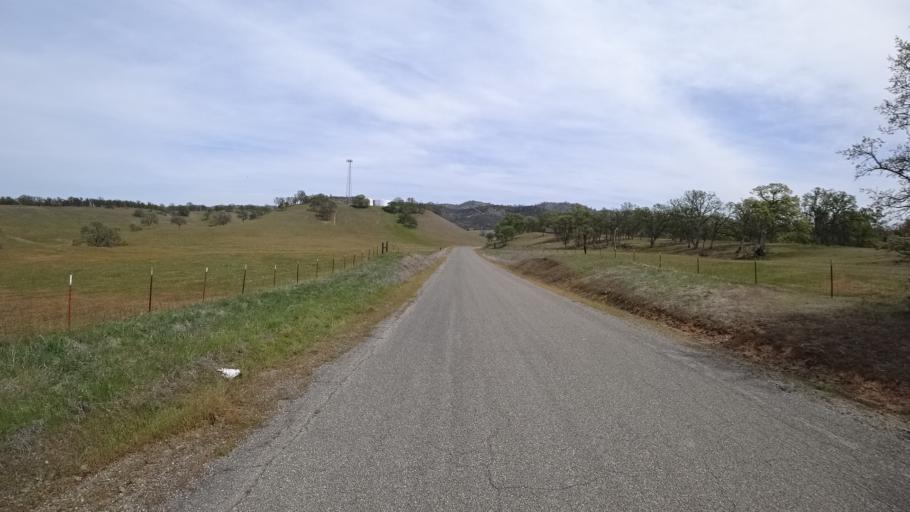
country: US
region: California
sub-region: Glenn County
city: Willows
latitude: 39.5949
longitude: -122.5513
